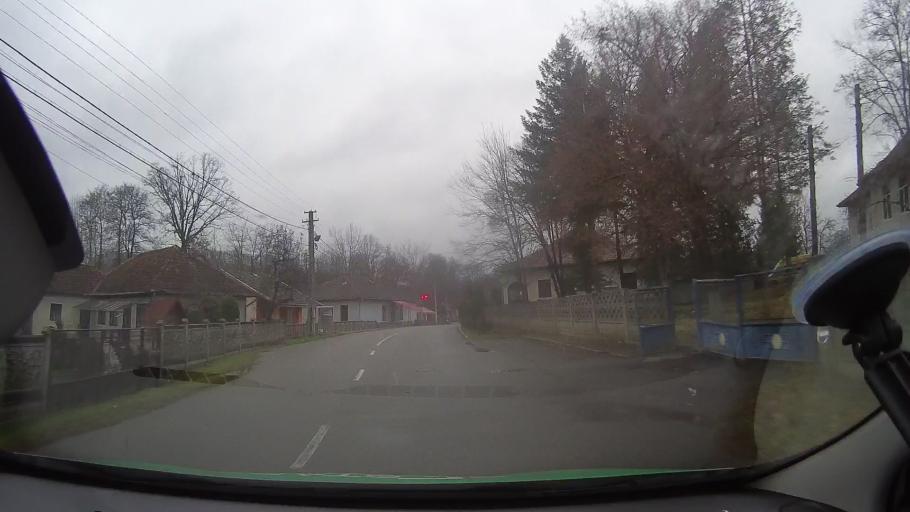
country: RO
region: Hunedoara
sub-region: Comuna Tomesti
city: Tomesti
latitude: 46.2133
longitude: 22.6651
